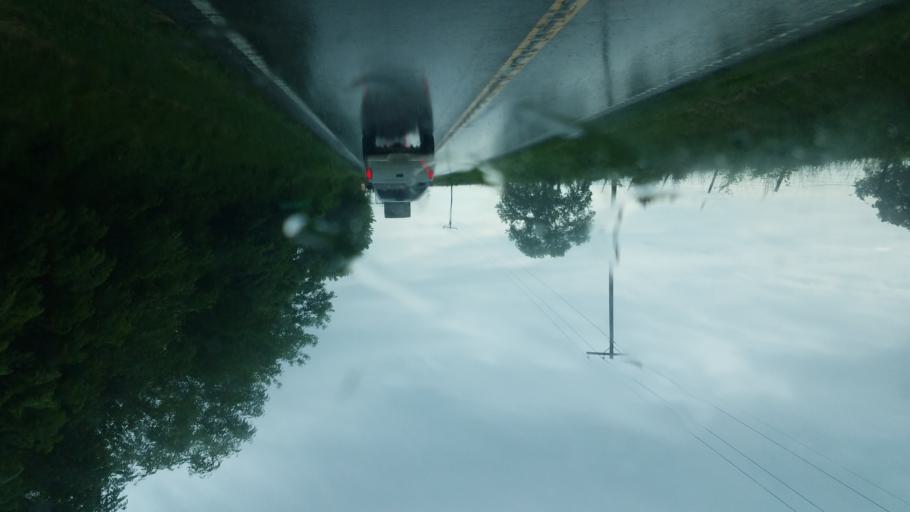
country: US
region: Missouri
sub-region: Cooper County
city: Boonville
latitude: 38.8897
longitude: -92.6541
